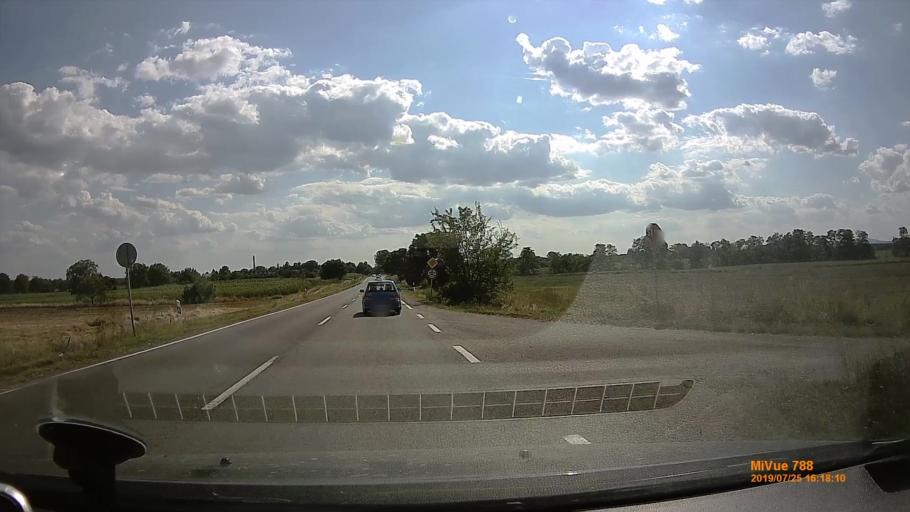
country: HU
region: Heves
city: Kal
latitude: 47.7627
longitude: 20.2637
